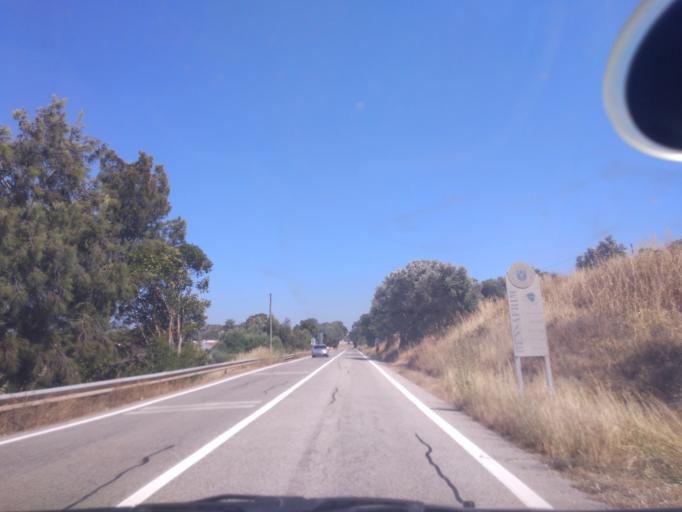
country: PT
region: Faro
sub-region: Lagos
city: Lagos
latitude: 37.1567
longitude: -8.7420
